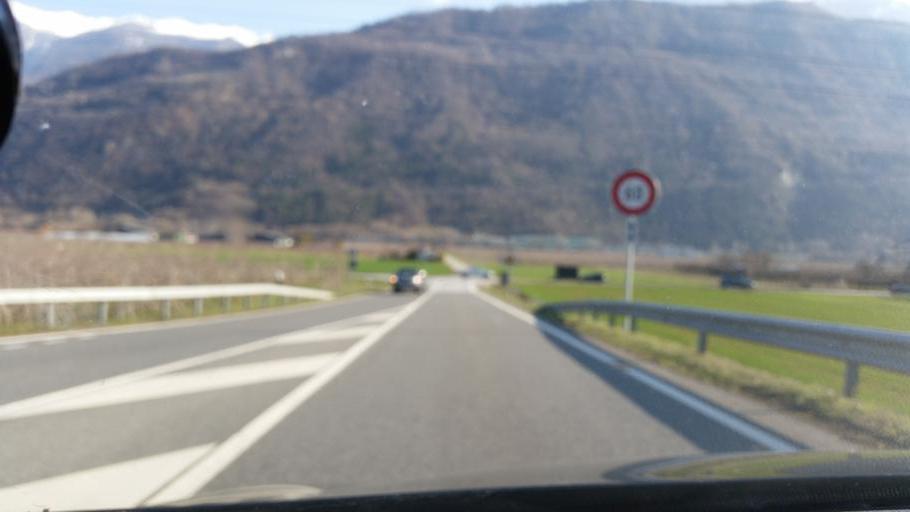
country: CH
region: Valais
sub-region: Conthey District
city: Vetroz
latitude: 46.2113
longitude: 7.2937
